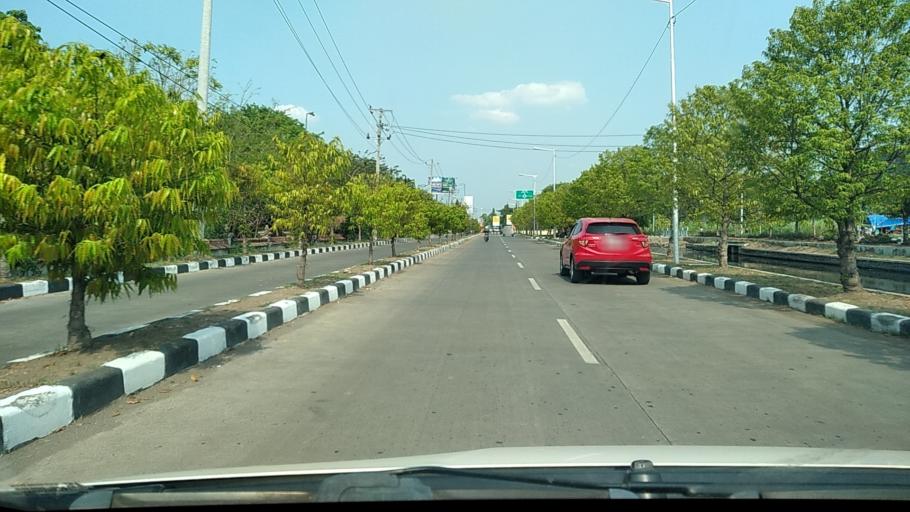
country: ID
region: Central Java
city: Semarang
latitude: -6.9626
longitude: 110.3886
